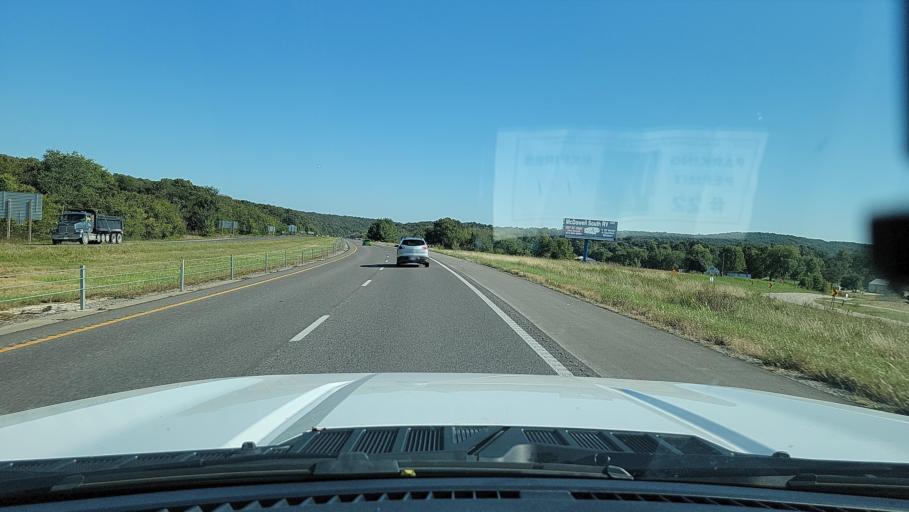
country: US
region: Missouri
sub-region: Sainte Genevieve County
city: Sainte Genevieve
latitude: 37.9286
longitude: -90.1115
